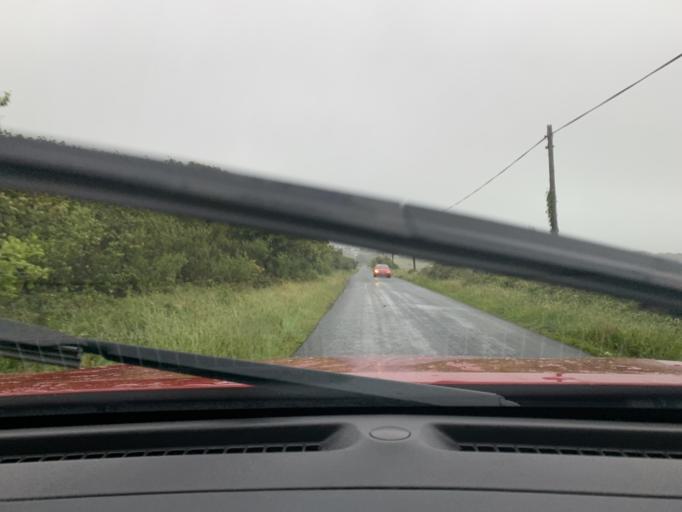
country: IE
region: Connaught
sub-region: County Leitrim
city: Kinlough
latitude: 54.4481
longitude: -8.4461
